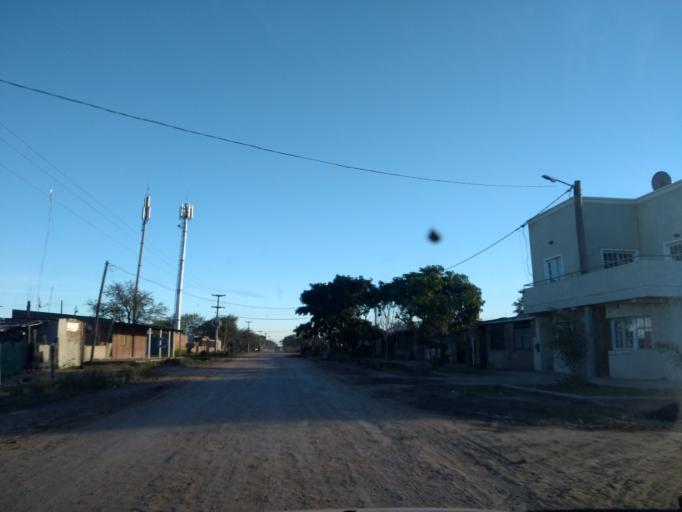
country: AR
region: Chaco
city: Puerto Vilelas
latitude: -27.4968
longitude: -58.9661
